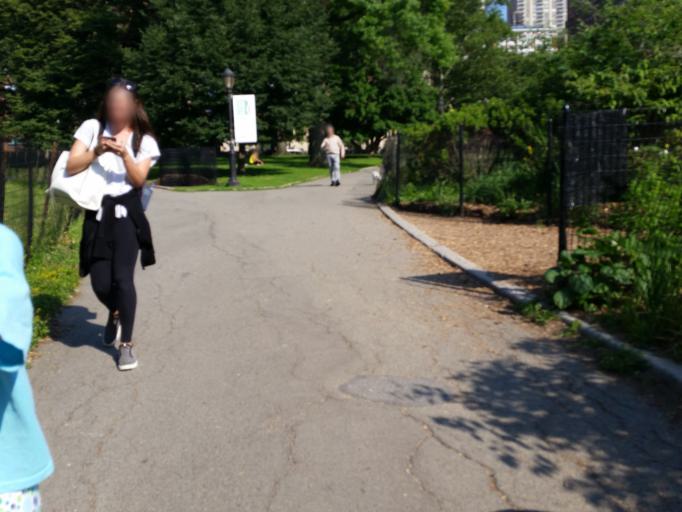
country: US
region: New Jersey
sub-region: Hudson County
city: Guttenberg
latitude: 40.7816
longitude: -73.9868
